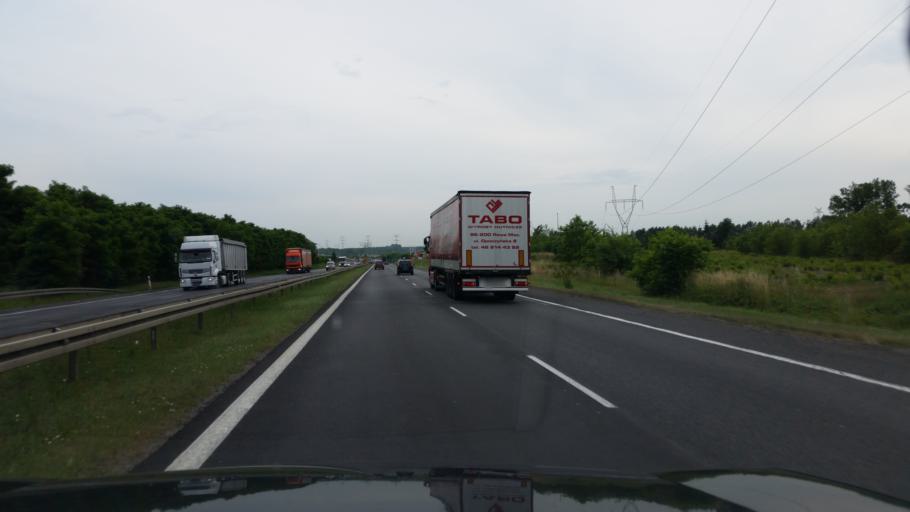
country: PL
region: Lodz Voivodeship
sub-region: Powiat radomszczanski
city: Radomsko
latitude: 51.1110
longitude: 19.3931
